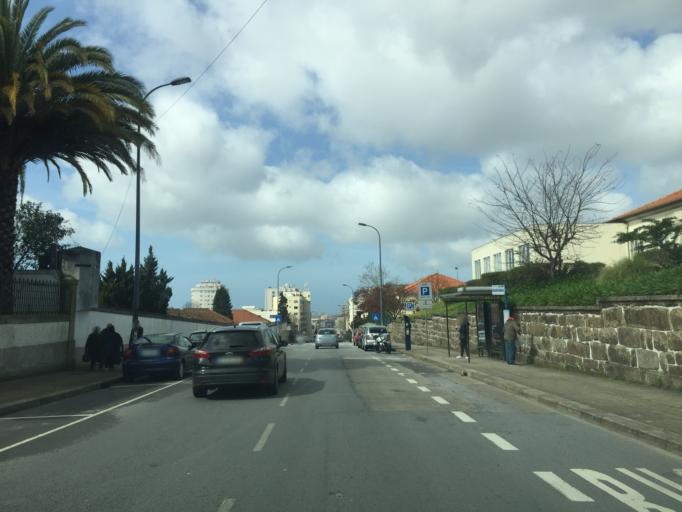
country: PT
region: Porto
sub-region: Porto
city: Porto
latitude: 41.1635
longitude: -8.6177
